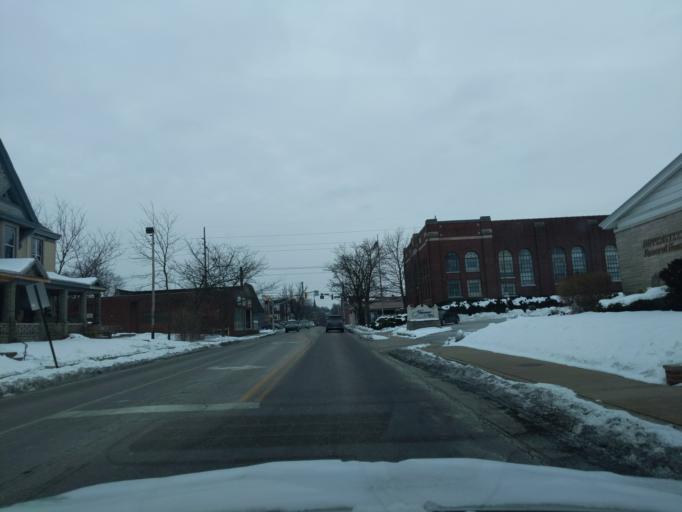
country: US
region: Indiana
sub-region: Tippecanoe County
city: Lafayette
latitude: 40.4257
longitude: -86.8870
